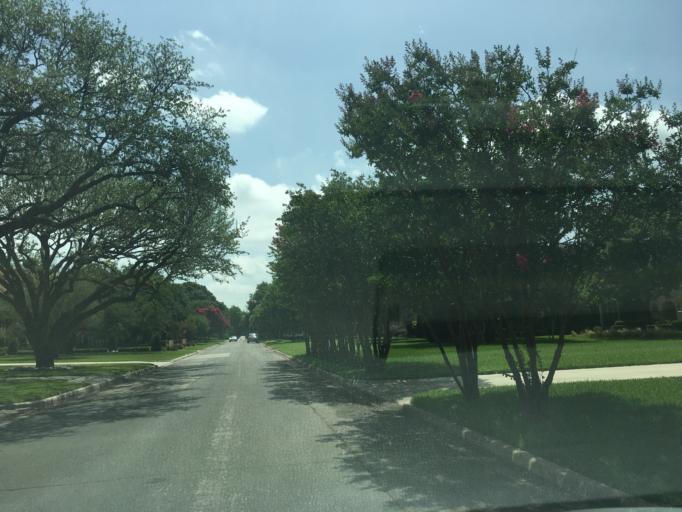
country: US
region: Texas
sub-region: Dallas County
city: University Park
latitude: 32.8781
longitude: -96.7975
